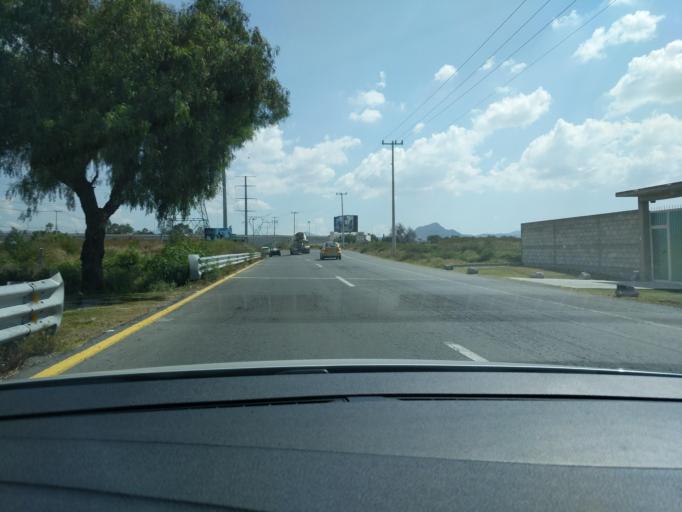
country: MX
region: Hidalgo
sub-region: Mineral de la Reforma
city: Rinconada de los Angeles
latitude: 20.0367
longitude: -98.7345
